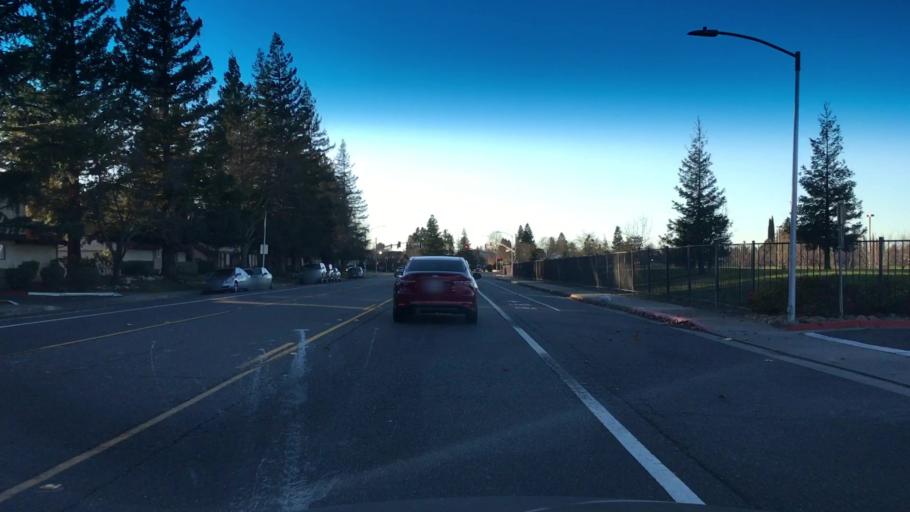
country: US
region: California
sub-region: Sacramento County
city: Laguna
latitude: 38.4498
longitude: -121.4235
